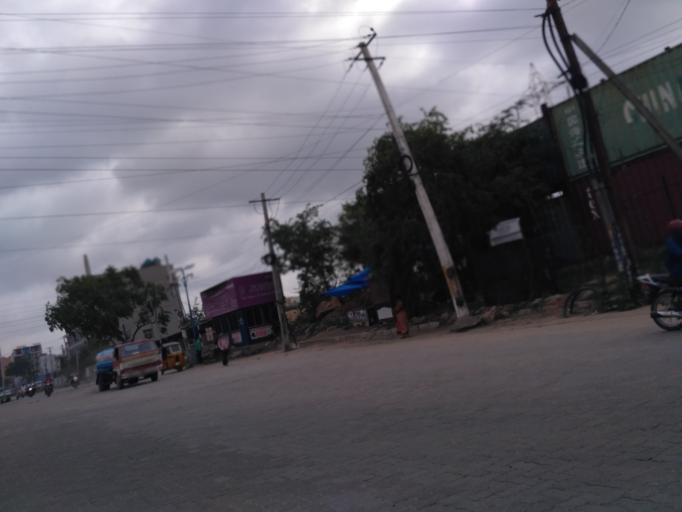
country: IN
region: Telangana
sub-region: Rangareddi
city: Kukatpalli
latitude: 17.4512
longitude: 78.3965
